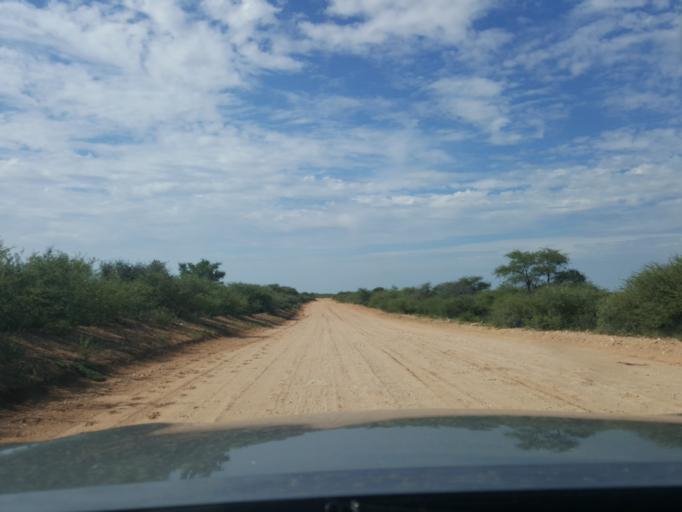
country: BW
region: Kweneng
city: Khudumelapye
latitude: -23.5795
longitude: 24.7233
